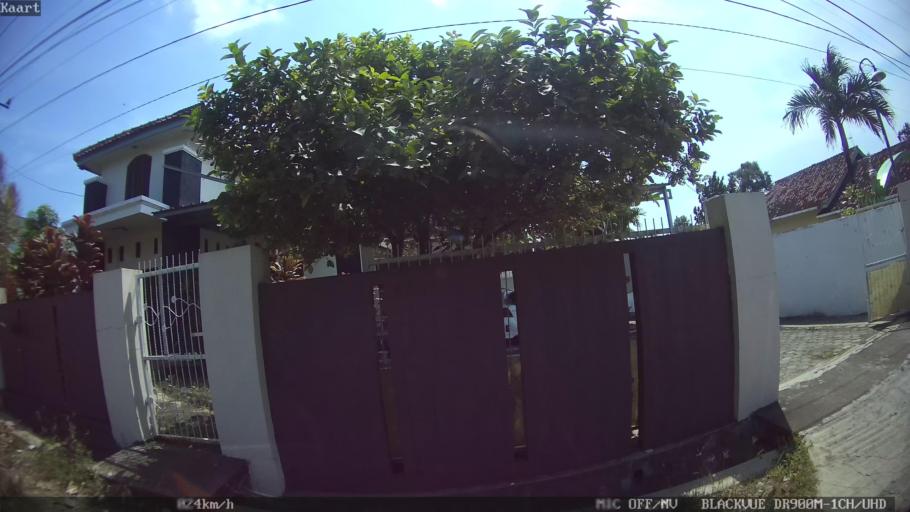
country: ID
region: Lampung
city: Kedaton
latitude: -5.3726
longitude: 105.2597
